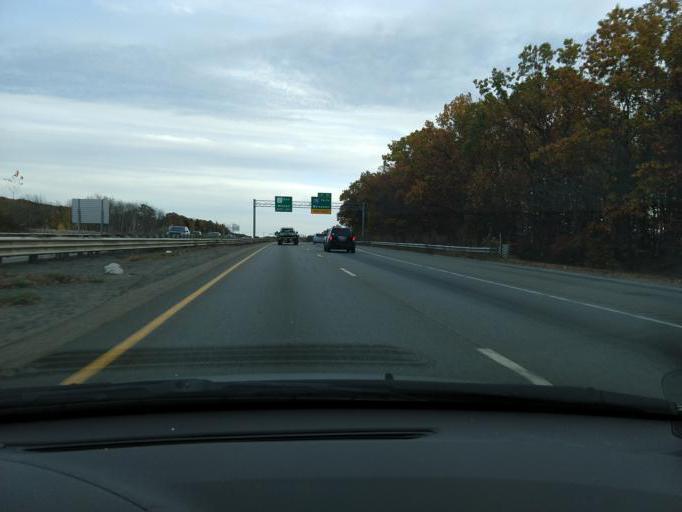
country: US
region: Massachusetts
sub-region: Worcester County
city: Leominster
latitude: 42.5325
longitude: -71.7378
